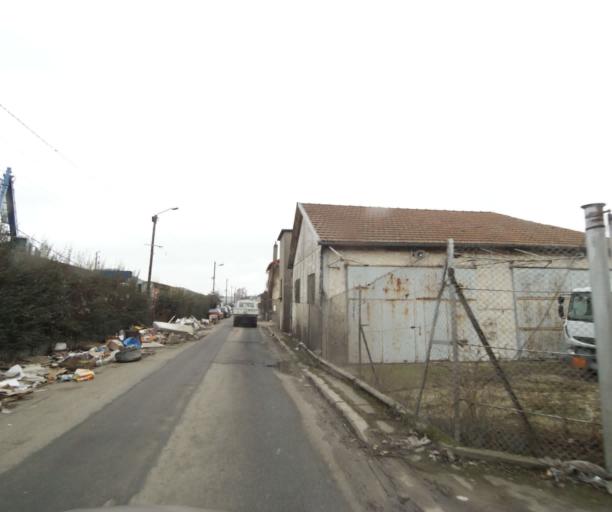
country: FR
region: Ile-de-France
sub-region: Departement du Val-de-Marne
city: Ablon-sur-Seine
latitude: 48.7342
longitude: 2.4322
